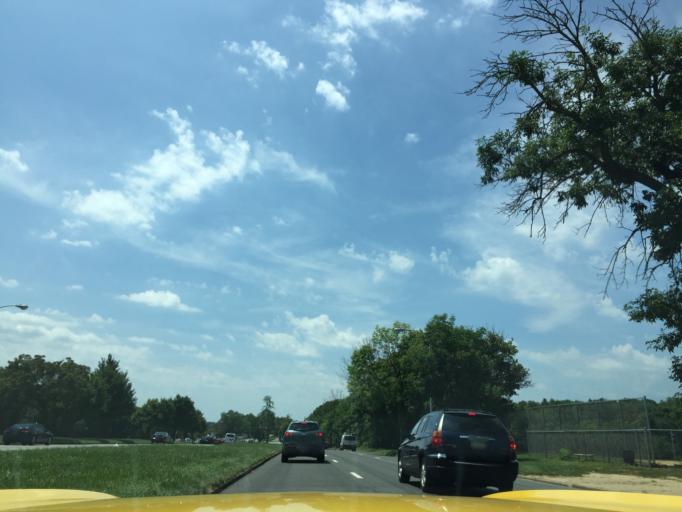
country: US
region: Pennsylvania
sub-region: Bucks County
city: Feasterville
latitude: 40.0908
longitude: -75.0194
